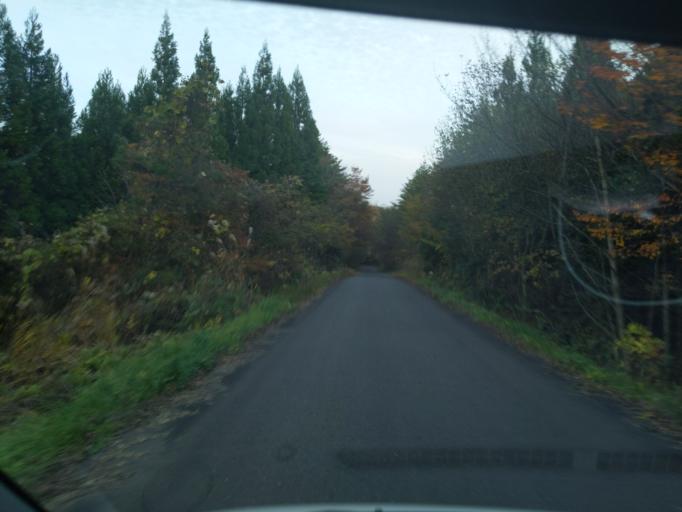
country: JP
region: Iwate
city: Ichinoseki
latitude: 39.0015
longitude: 141.0341
